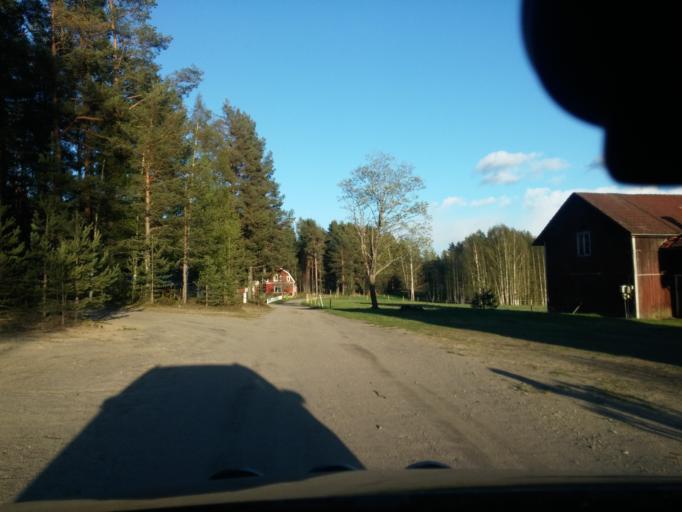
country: SE
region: Gaevleborg
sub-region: Bollnas Kommun
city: Kilafors
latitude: 61.3735
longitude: 16.6228
